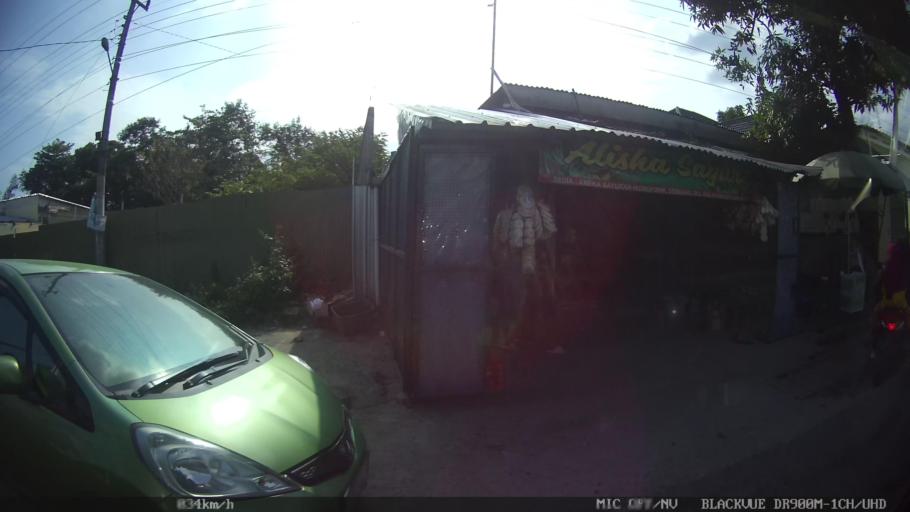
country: ID
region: Daerah Istimewa Yogyakarta
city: Depok
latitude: -7.7448
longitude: 110.4502
